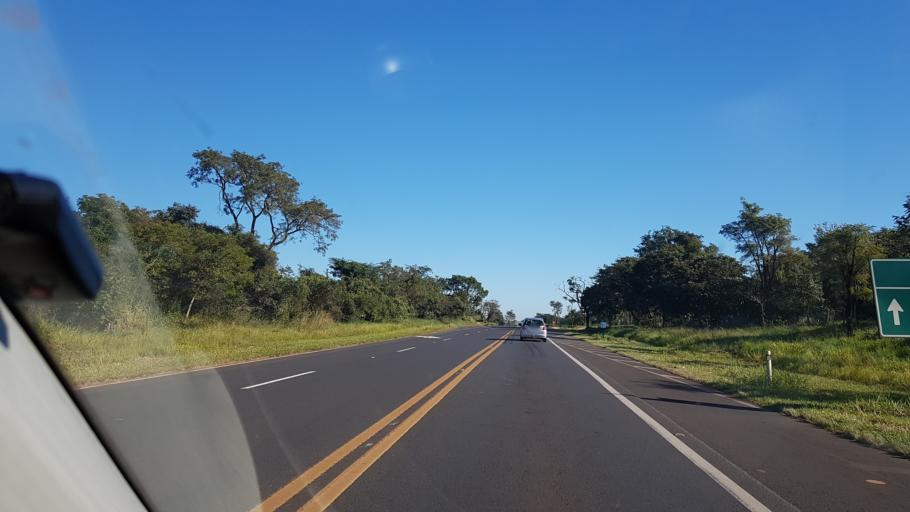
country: BR
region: Sao Paulo
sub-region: Assis
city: Assis
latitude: -22.6199
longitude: -50.4546
